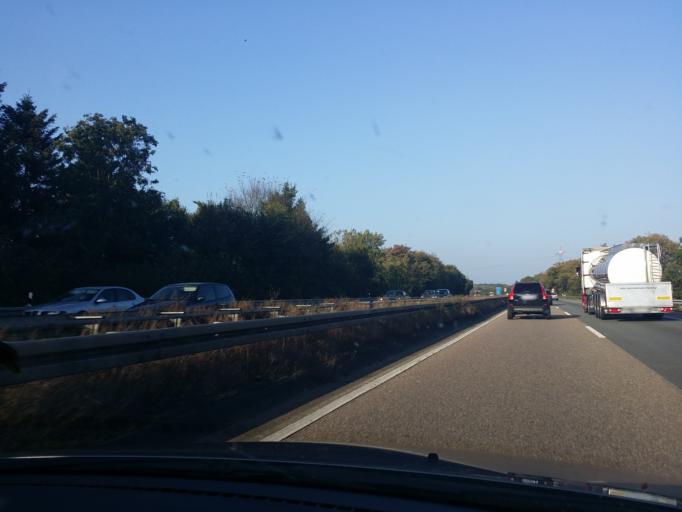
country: DE
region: Lower Saxony
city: Hasbergen
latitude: 52.2531
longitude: 7.9156
